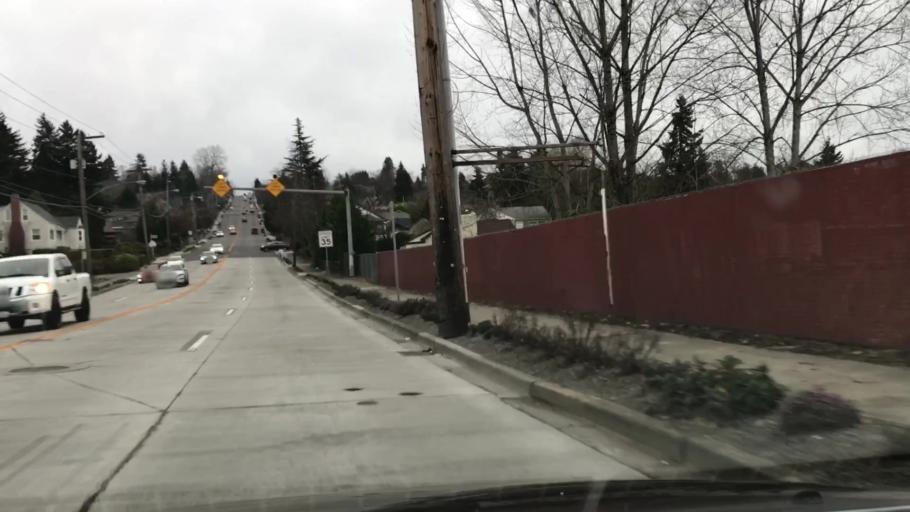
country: US
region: Washington
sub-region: King County
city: Kent
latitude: 47.3866
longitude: -122.2287
